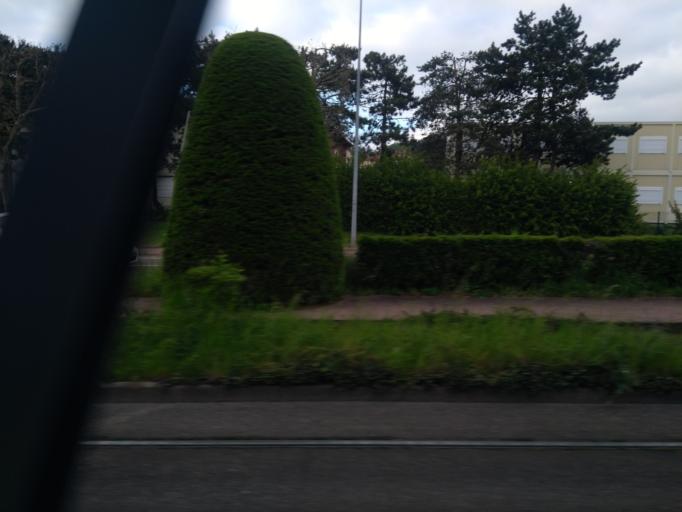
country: FR
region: Rhone-Alpes
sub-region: Departement de la Loire
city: Saint-Priest-en-Jarez
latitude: 45.4750
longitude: 4.3668
